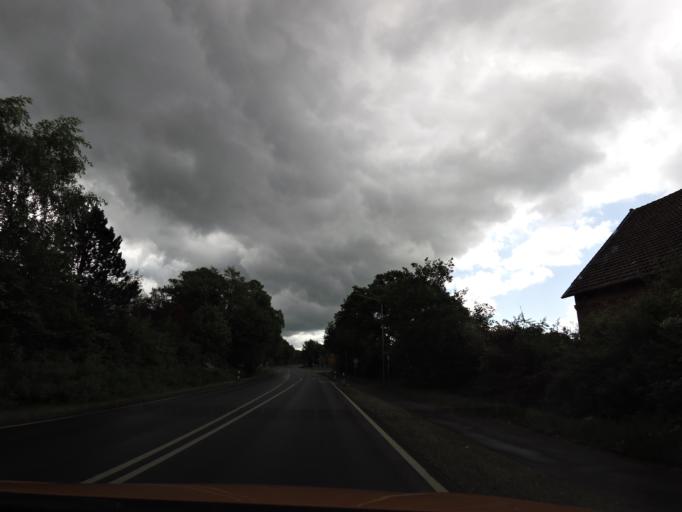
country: DE
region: Lower Saxony
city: Hude
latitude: 53.0977
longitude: 8.4923
